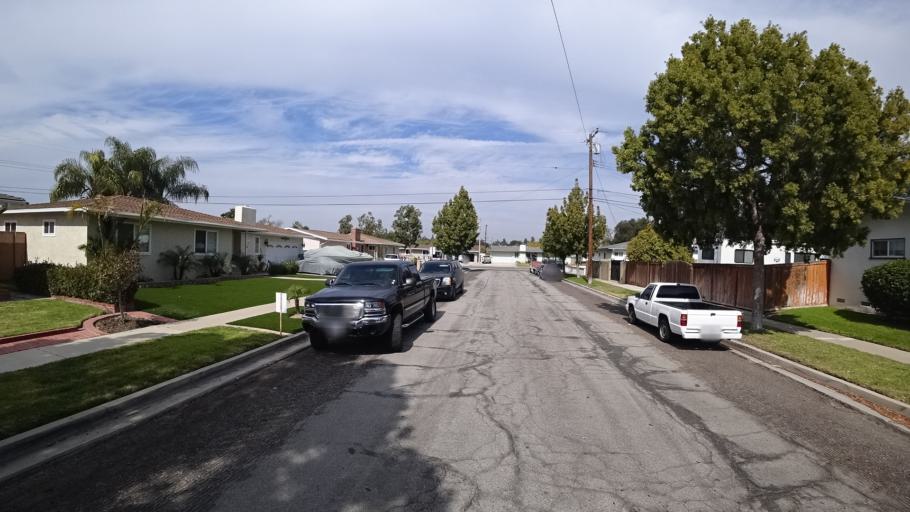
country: US
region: California
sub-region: Orange County
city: Garden Grove
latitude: 33.8099
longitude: -117.9533
